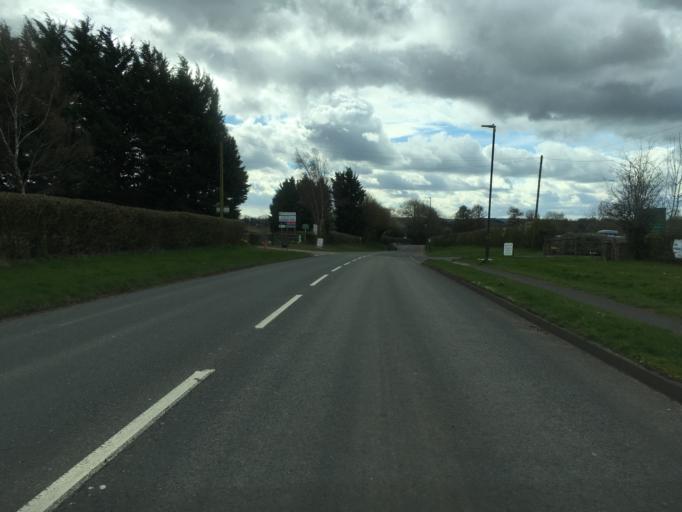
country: GB
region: England
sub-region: Gloucestershire
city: Coleford
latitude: 51.8012
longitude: -2.6030
